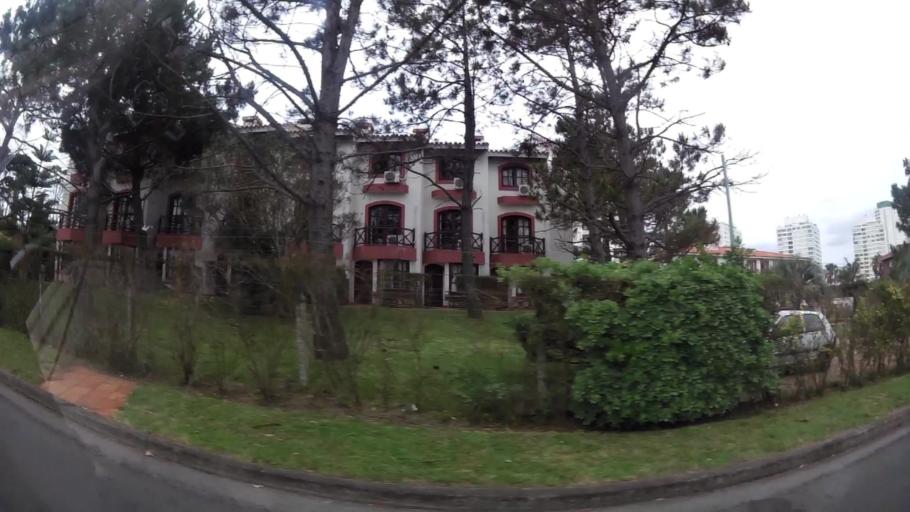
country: UY
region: Maldonado
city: Maldonado
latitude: -34.9240
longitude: -54.9627
